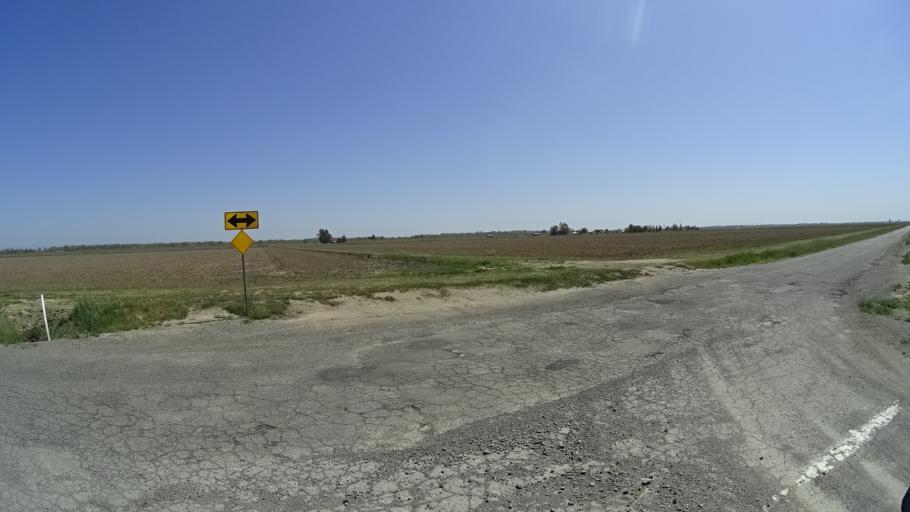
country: US
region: California
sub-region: Glenn County
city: Hamilton City
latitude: 39.5727
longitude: -122.0280
